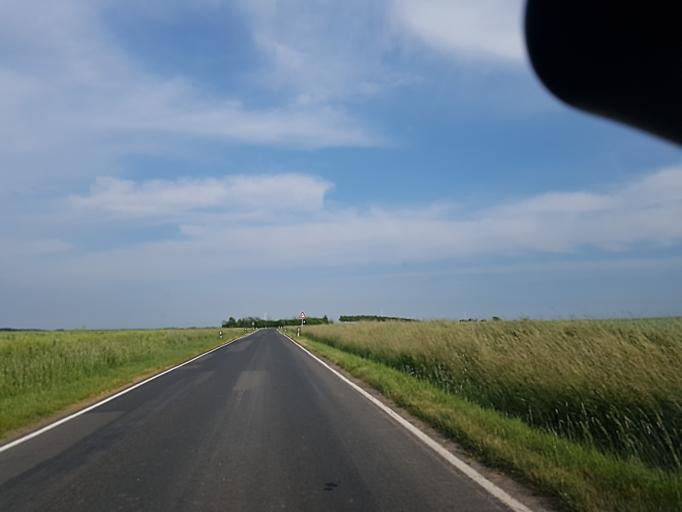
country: DE
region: Saxony-Anhalt
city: Kropstadt
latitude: 51.9866
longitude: 12.8000
